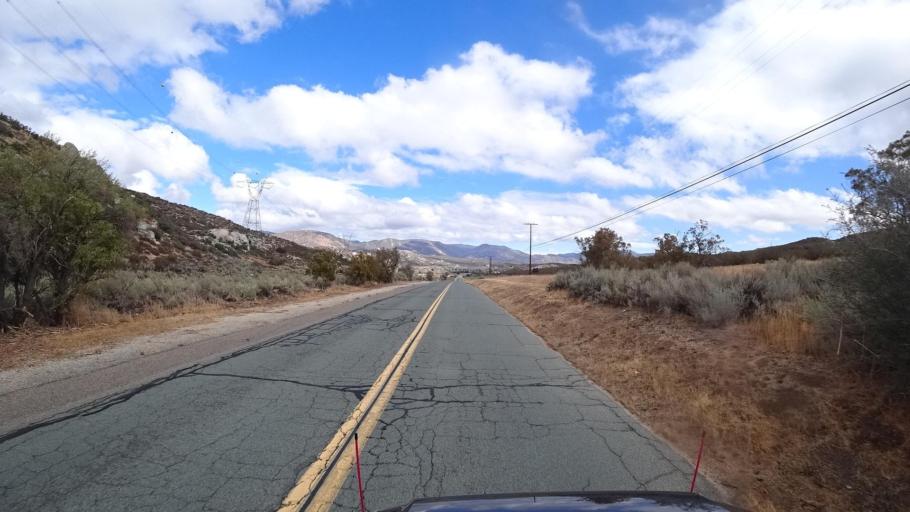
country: US
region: California
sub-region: San Diego County
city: Campo
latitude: 32.7104
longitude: -116.4309
